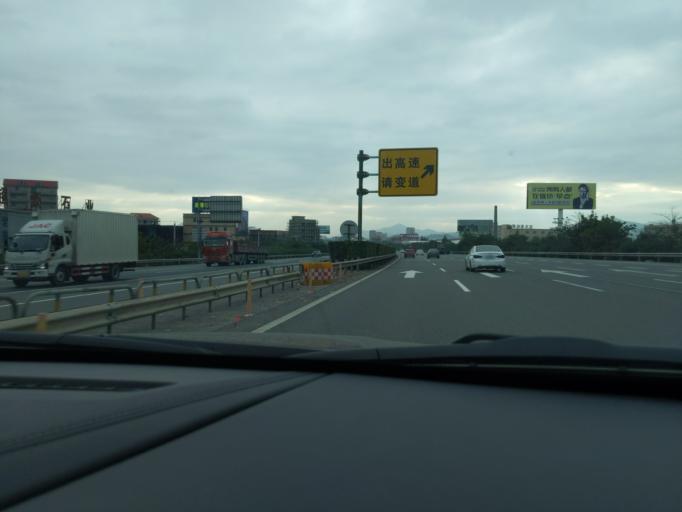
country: CN
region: Fujian
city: Anhai
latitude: 24.7457
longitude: 118.4293
